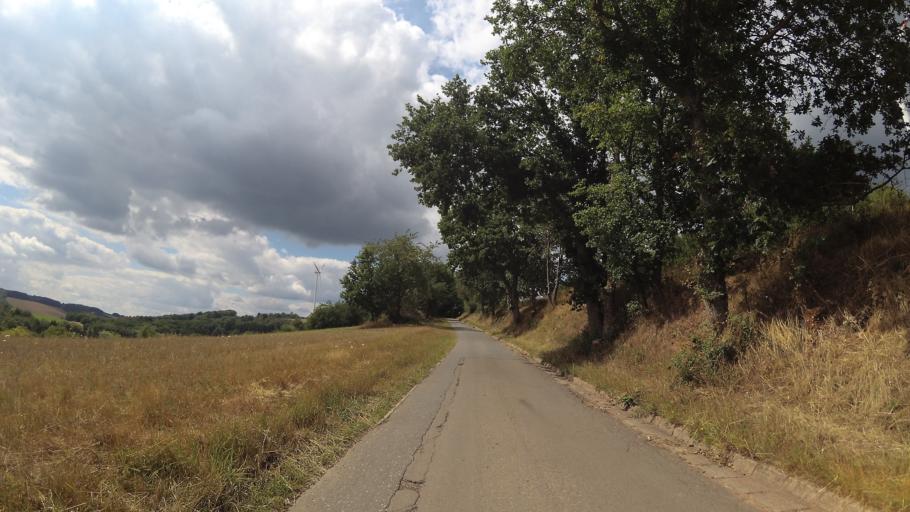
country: DE
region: Rheinland-Pfalz
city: Breitenbach
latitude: 49.4713
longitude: 7.2386
